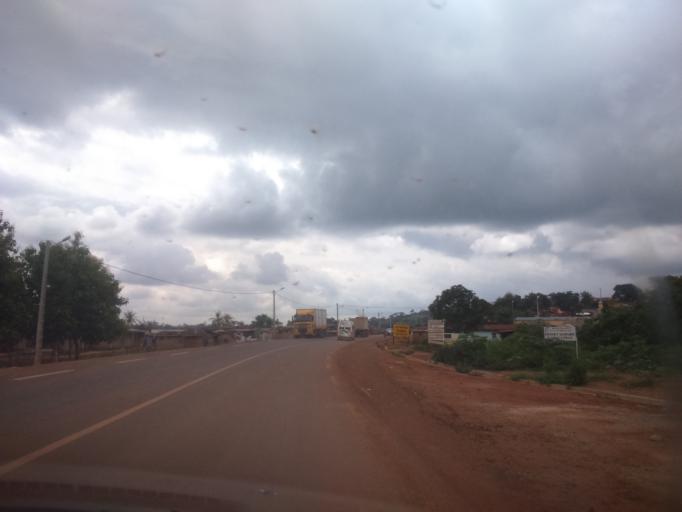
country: CI
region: Moyen-Comoe
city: Abengourou
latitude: 6.6389
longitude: -3.7138
